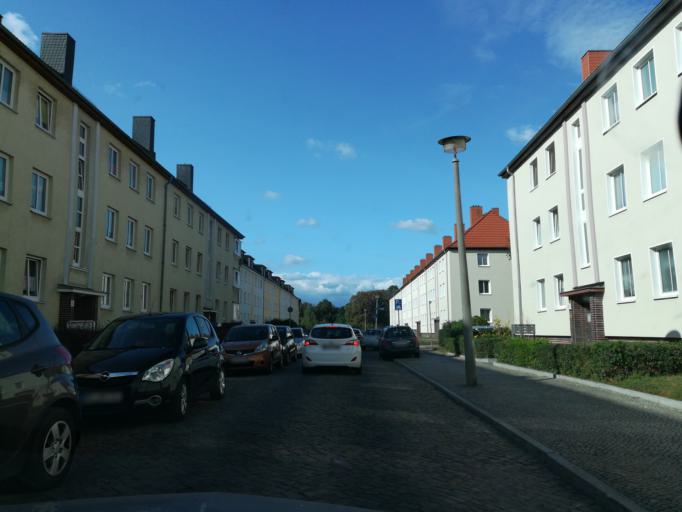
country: DE
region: Saxony-Anhalt
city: Magdeburg
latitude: 52.1301
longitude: 11.5979
